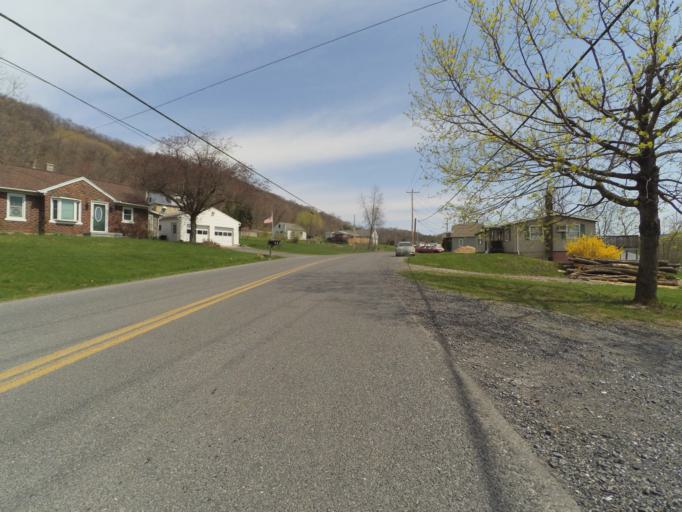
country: US
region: Pennsylvania
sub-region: Clinton County
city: Avis
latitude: 41.1775
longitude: -77.3481
